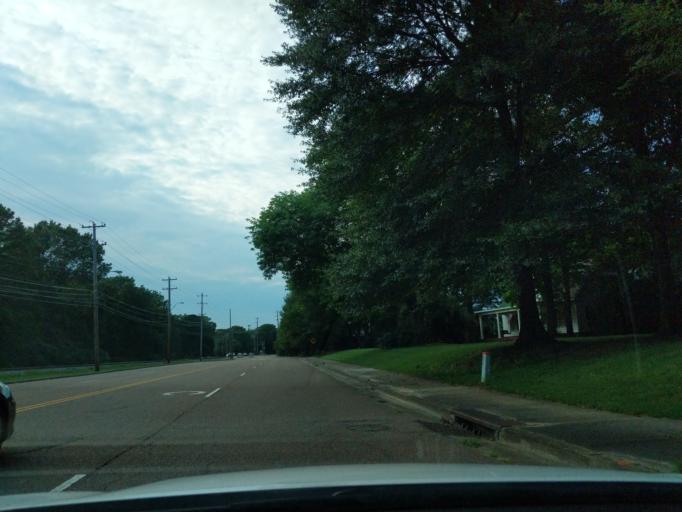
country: US
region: Tennessee
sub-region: Shelby County
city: Germantown
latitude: 35.0786
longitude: -89.7997
